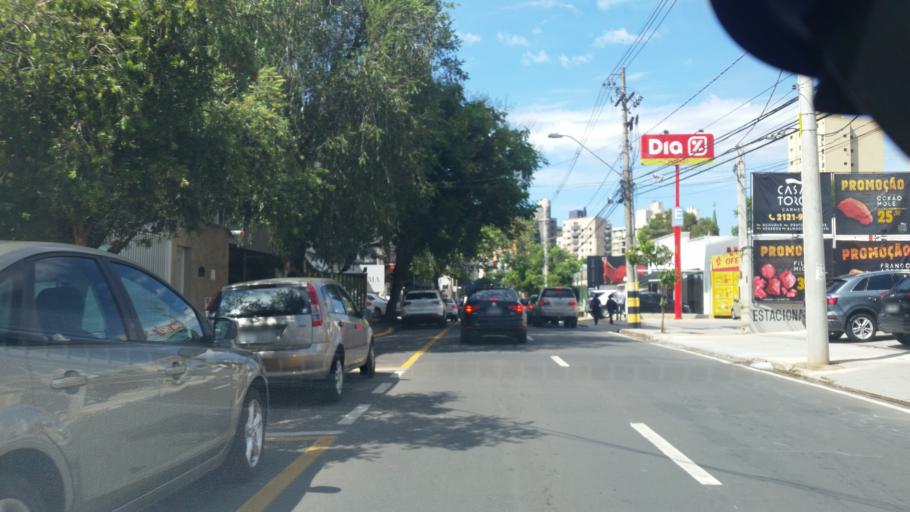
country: BR
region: Sao Paulo
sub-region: Campinas
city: Campinas
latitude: -22.8941
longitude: -47.0566
